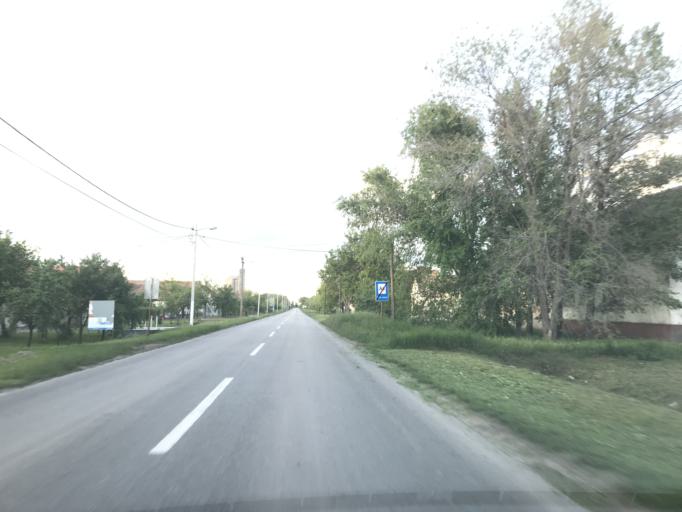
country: RS
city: Cestereg
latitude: 45.5640
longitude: 20.5330
